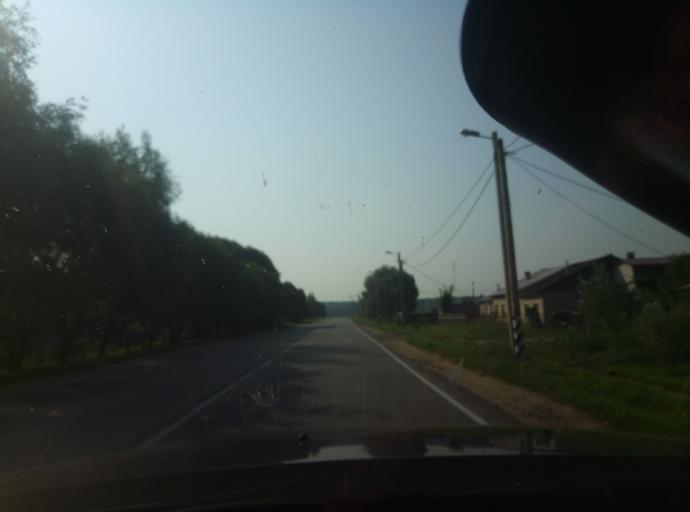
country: RU
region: Kaluga
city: Zhukovo
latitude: 54.9870
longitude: 36.7642
